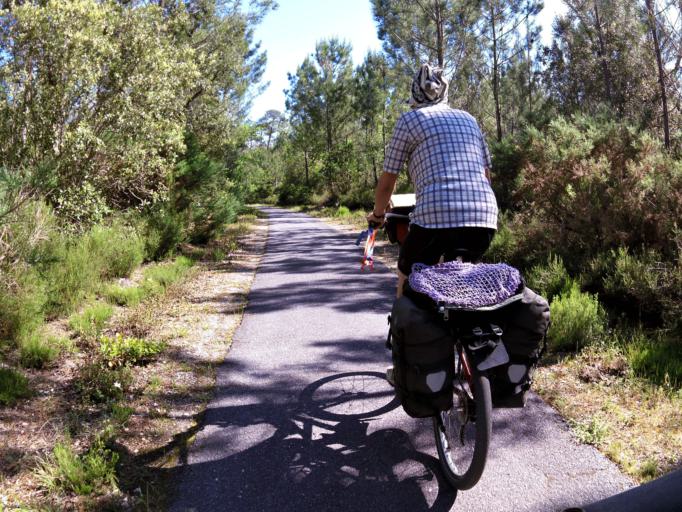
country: FR
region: Aquitaine
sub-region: Departement de la Gironde
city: Lacanau
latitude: 45.0349
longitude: -1.1557
